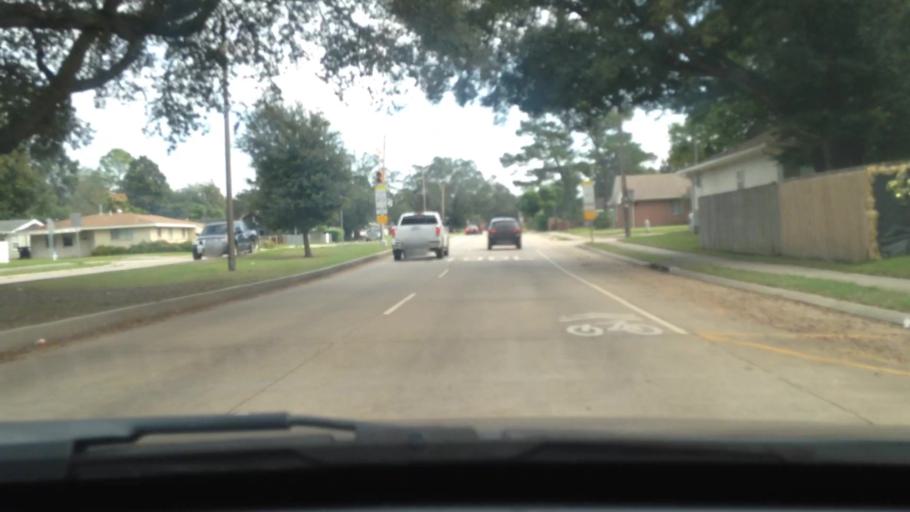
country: US
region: Louisiana
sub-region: Jefferson Parish
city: Terrytown
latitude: 29.9237
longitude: -90.0060
